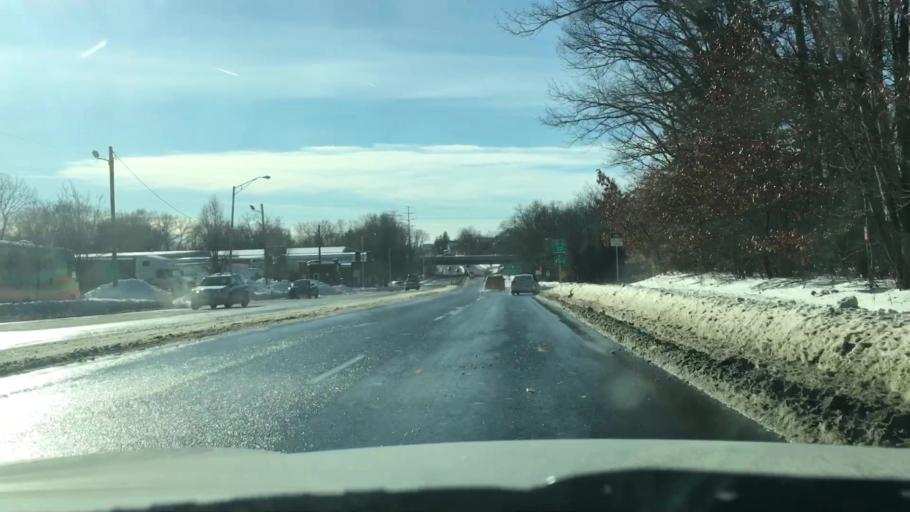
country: US
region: Massachusetts
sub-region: Hampden County
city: Chicopee
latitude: 42.1471
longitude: -72.5451
